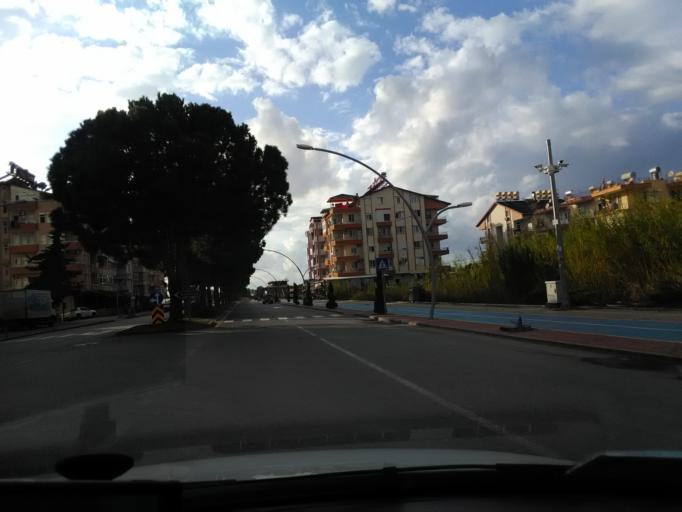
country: TR
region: Antalya
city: Gazipasa
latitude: 36.2650
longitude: 32.2890
